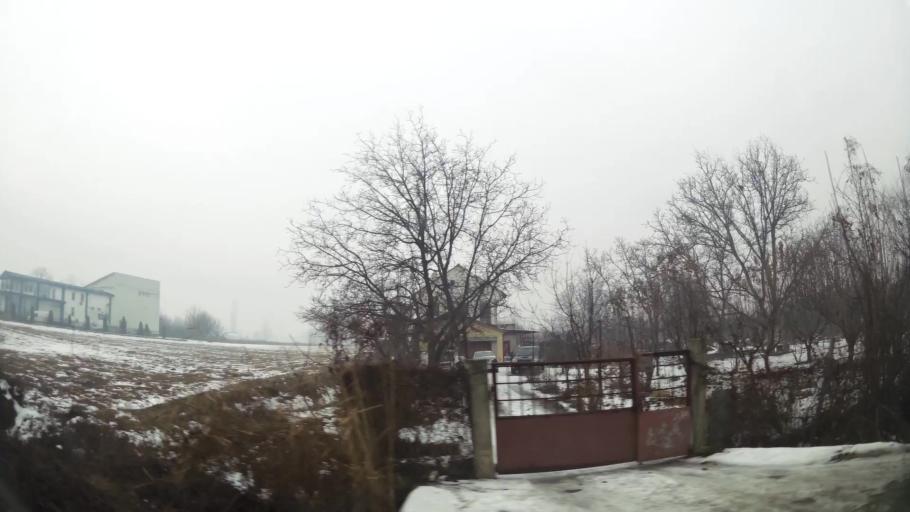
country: MK
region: Ilinden
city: Idrizovo
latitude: 41.9571
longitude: 21.5821
